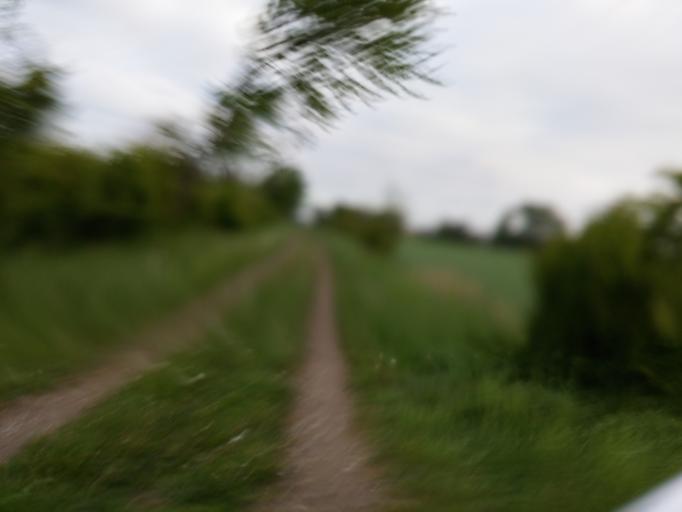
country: DK
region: South Denmark
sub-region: Kerteminde Kommune
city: Munkebo
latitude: 55.4321
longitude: 10.5420
